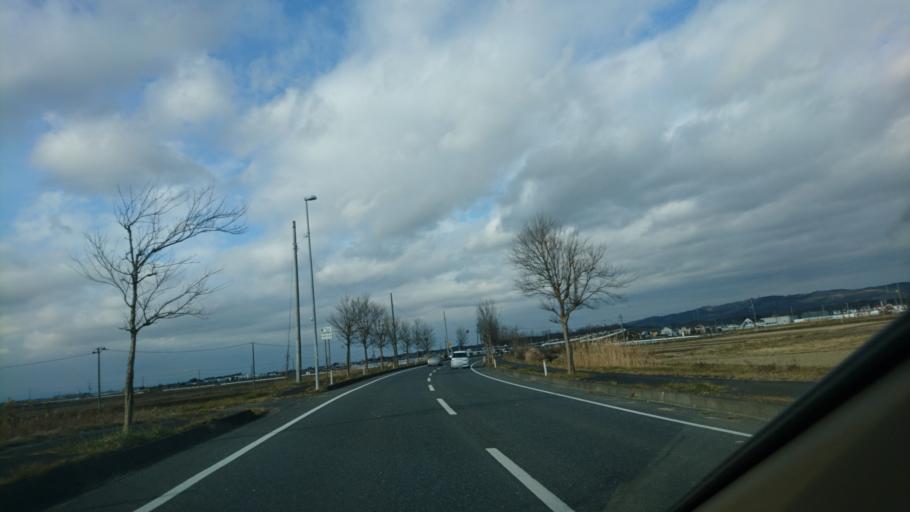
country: JP
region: Miyagi
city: Wakuya
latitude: 38.5418
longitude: 141.1091
